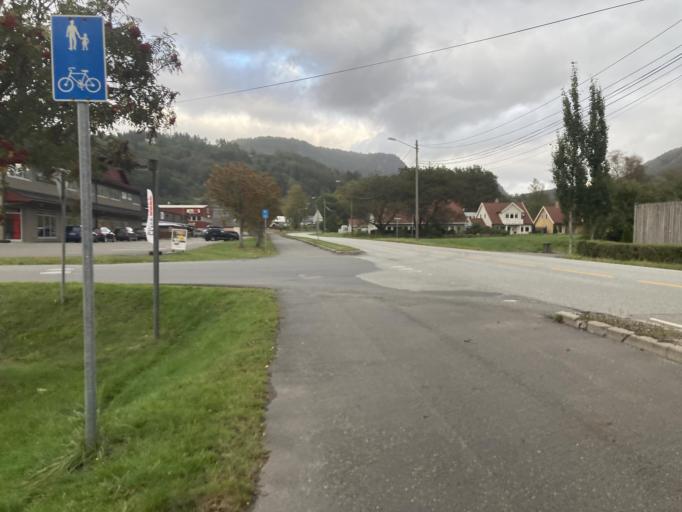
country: NO
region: Vest-Agder
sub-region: Kvinesdal
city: Liknes
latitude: 58.3212
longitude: 6.9665
